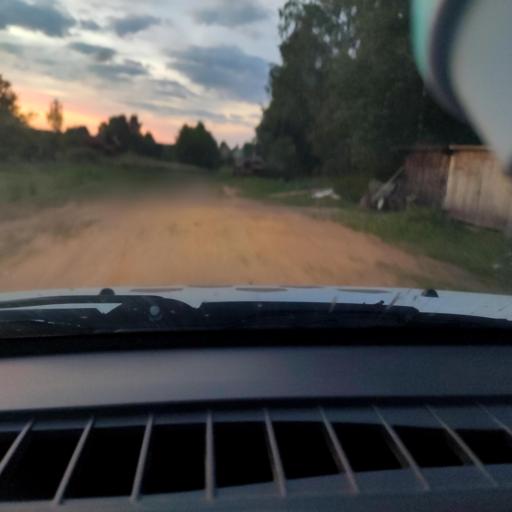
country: RU
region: Kirov
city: Darovskoy
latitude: 58.9910
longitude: 47.8679
